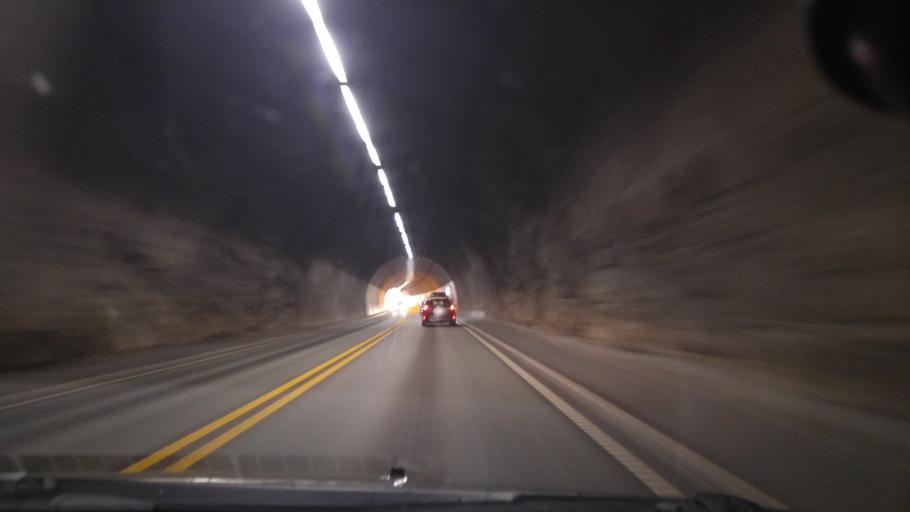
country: NO
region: Sor-Trondelag
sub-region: Malvik
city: Malvik
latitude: 63.4219
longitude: 10.6104
